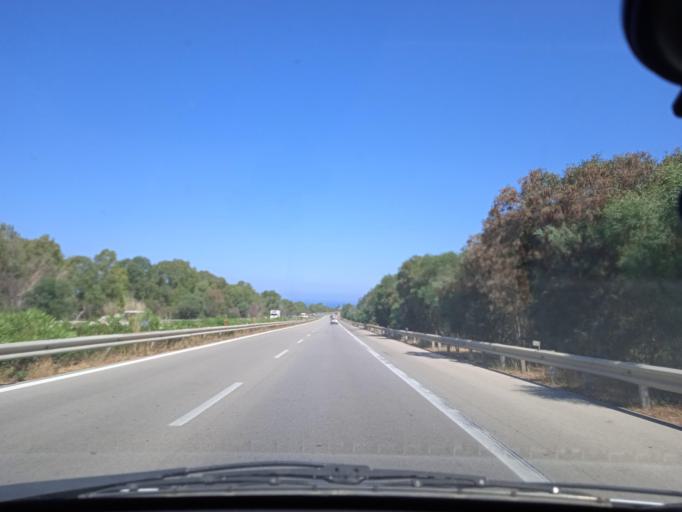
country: IT
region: Sicily
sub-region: Palermo
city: Agliandroni-Paternella
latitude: 38.1196
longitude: 13.0812
